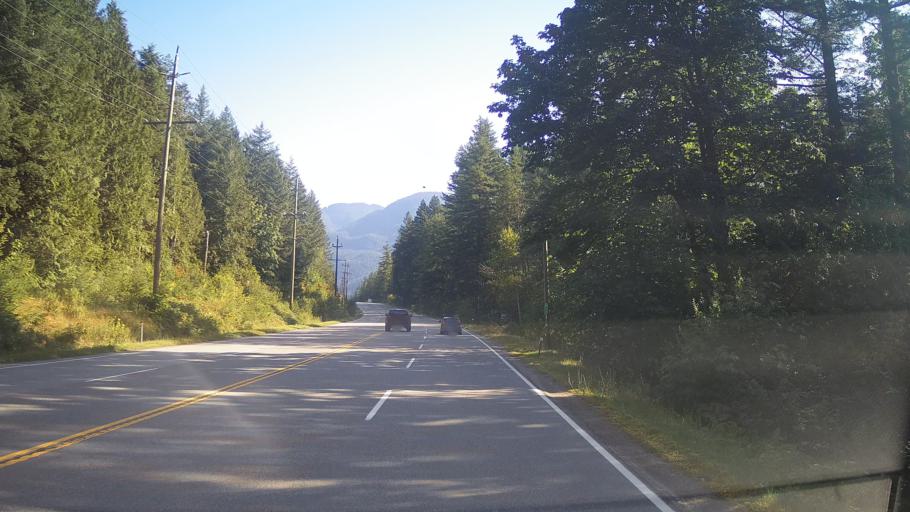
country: CA
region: British Columbia
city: Hope
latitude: 49.4648
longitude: -121.4324
